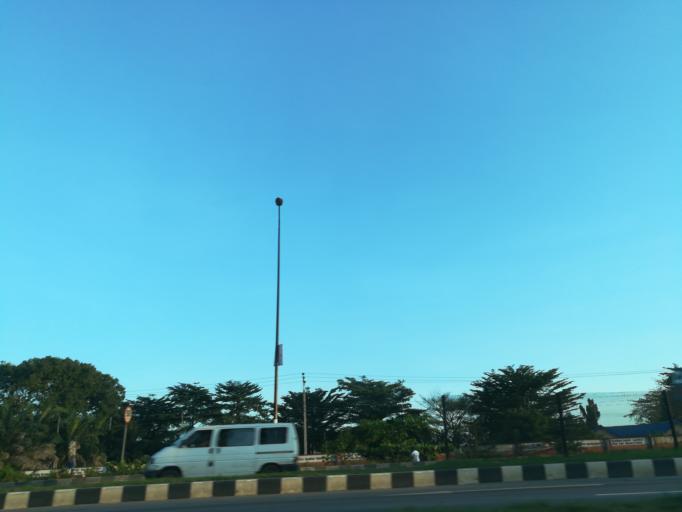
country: NG
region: Lagos
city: Ebute Ikorodu
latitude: 6.6205
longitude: 3.4798
